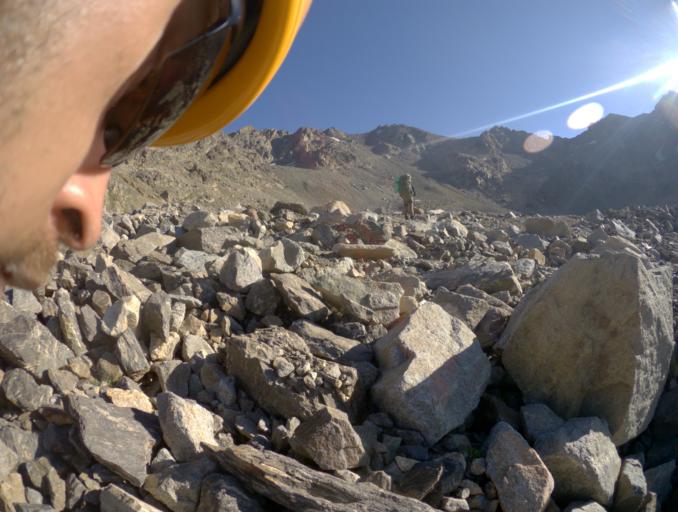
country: RU
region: Kabardino-Balkariya
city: Terskol
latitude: 43.3235
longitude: 42.5278
